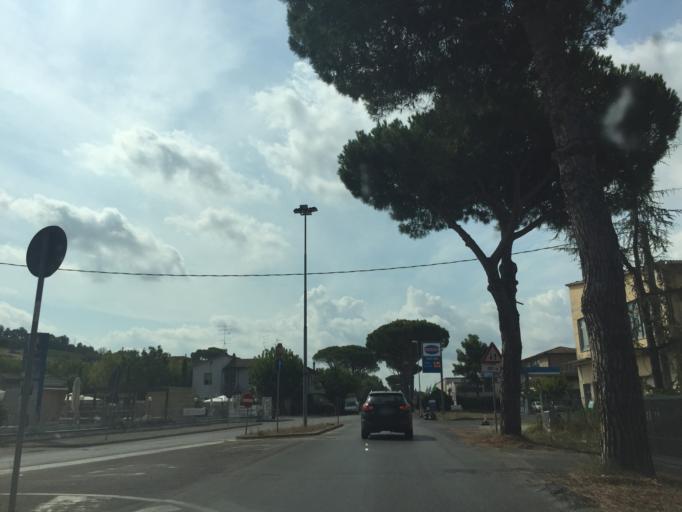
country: IT
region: Tuscany
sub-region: Province of Florence
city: Cerreto Guidi
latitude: 43.7425
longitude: 10.9012
